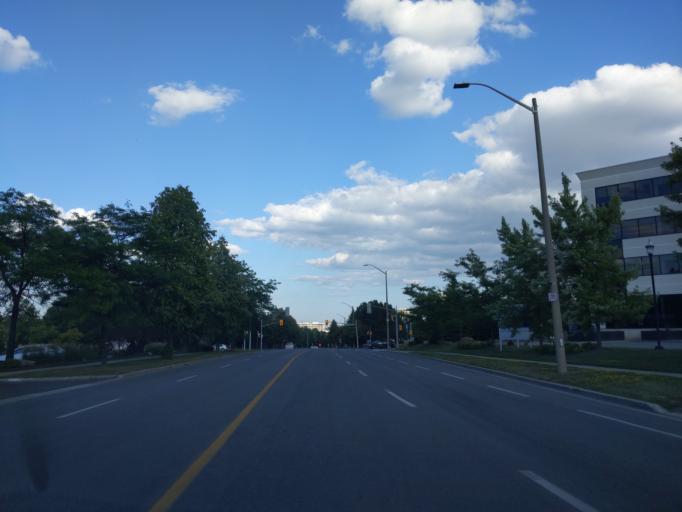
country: CA
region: Ontario
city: Markham
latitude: 43.8603
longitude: -79.3399
